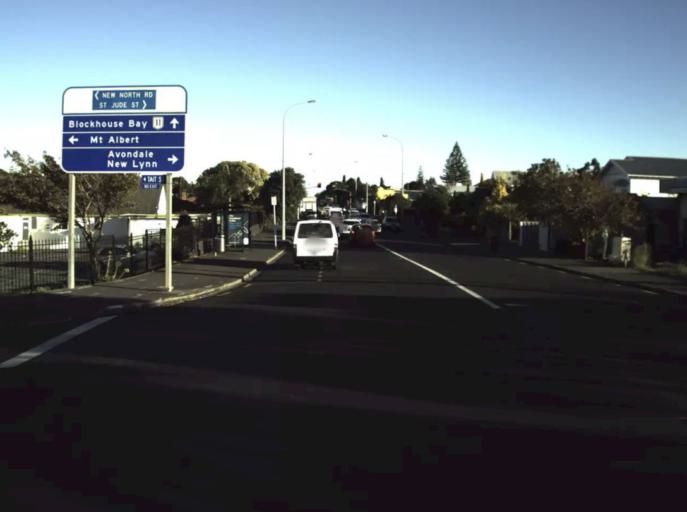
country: NZ
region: Auckland
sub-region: Auckland
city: Rosebank
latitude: -36.8947
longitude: 174.7010
